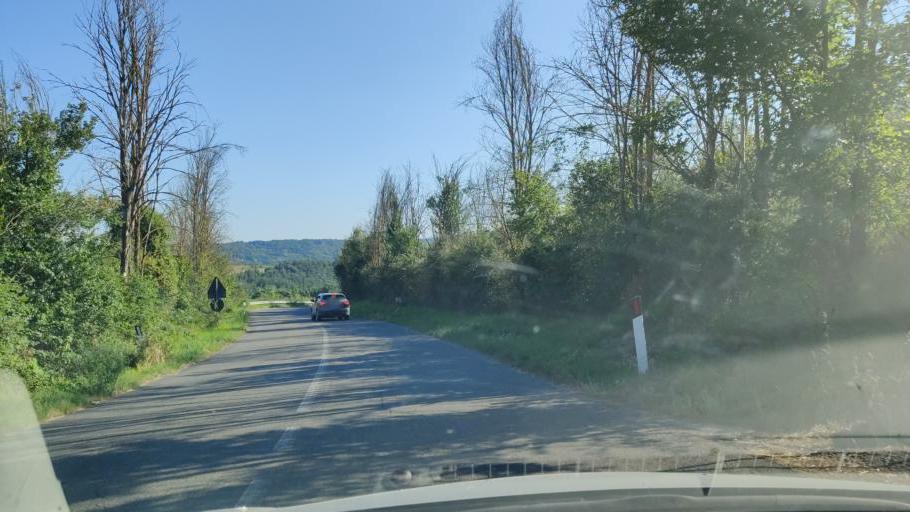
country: IT
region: Umbria
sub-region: Provincia di Terni
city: Penna in Teverina
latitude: 42.4862
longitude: 12.3695
